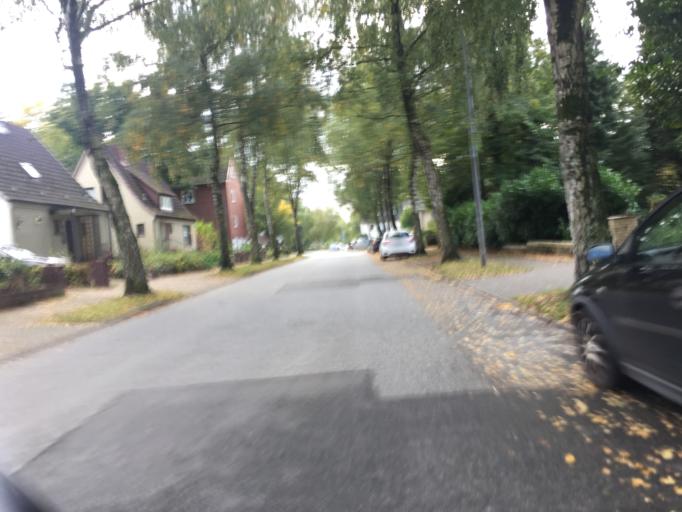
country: DE
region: Schleswig-Holstein
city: Itzehoe
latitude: 53.9419
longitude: 9.5084
